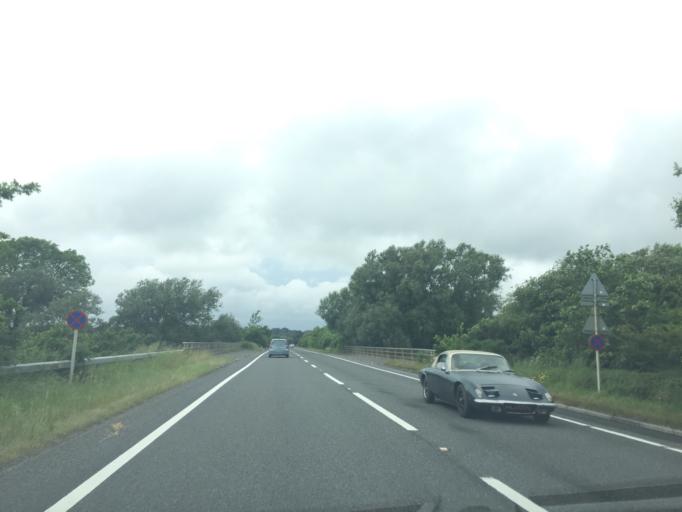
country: GB
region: England
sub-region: Dorset
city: Wareham
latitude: 50.6765
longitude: -2.1160
